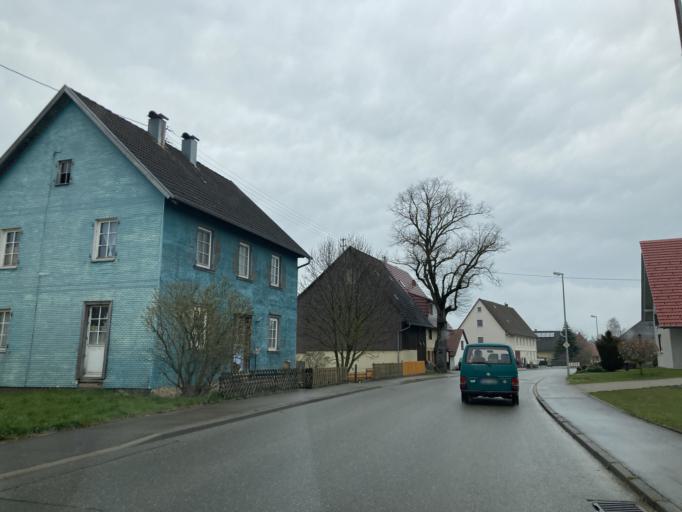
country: DE
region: Baden-Wuerttemberg
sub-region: Freiburg Region
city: Seedorf
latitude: 48.2667
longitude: 8.4807
